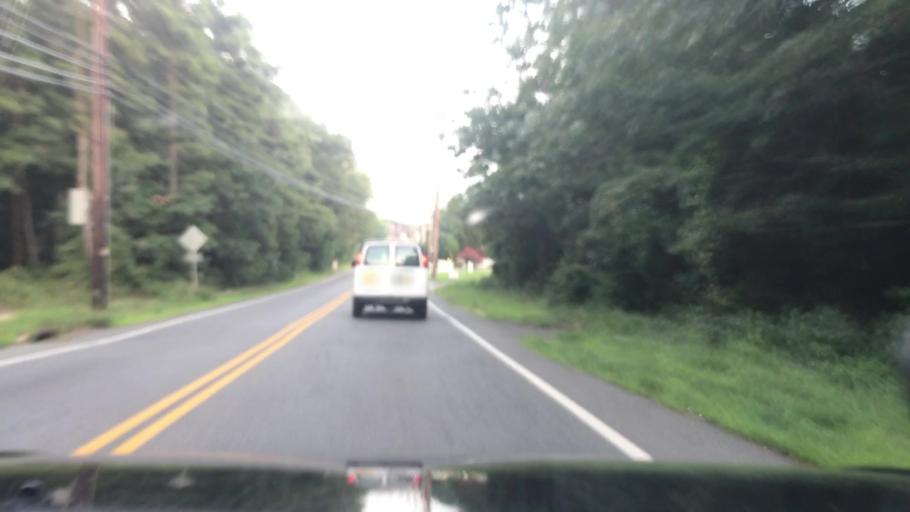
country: US
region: New Jersey
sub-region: Ocean County
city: Lakewood
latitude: 40.0580
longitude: -74.2262
